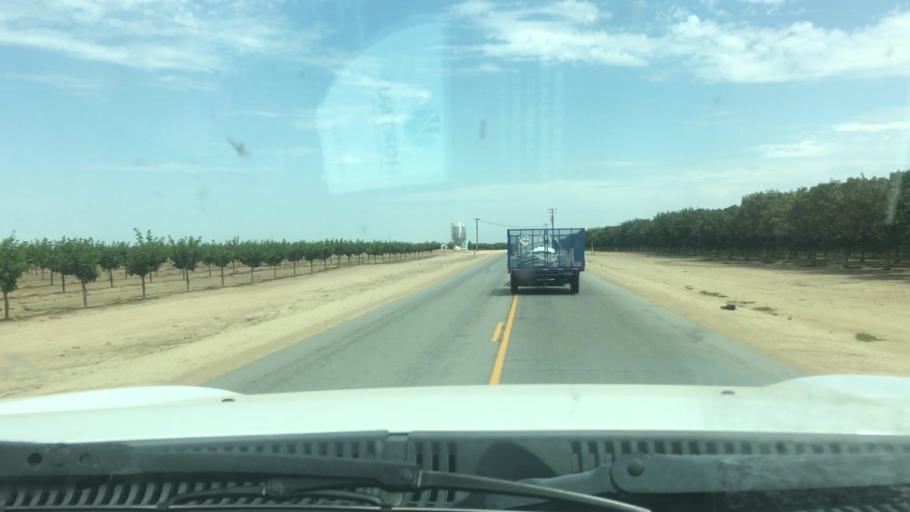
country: US
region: California
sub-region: Kern County
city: McFarland
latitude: 35.5887
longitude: -119.1510
